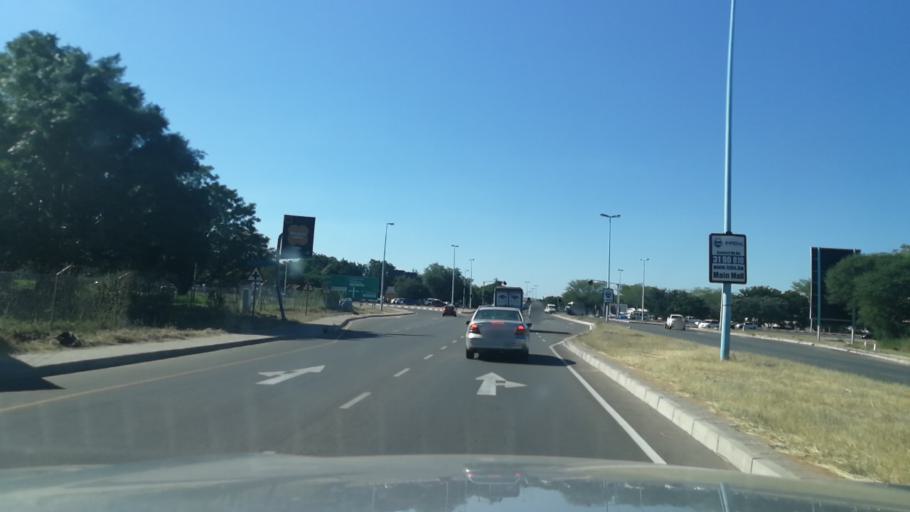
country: BW
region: South East
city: Gaborone
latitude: -24.6737
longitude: 25.9232
